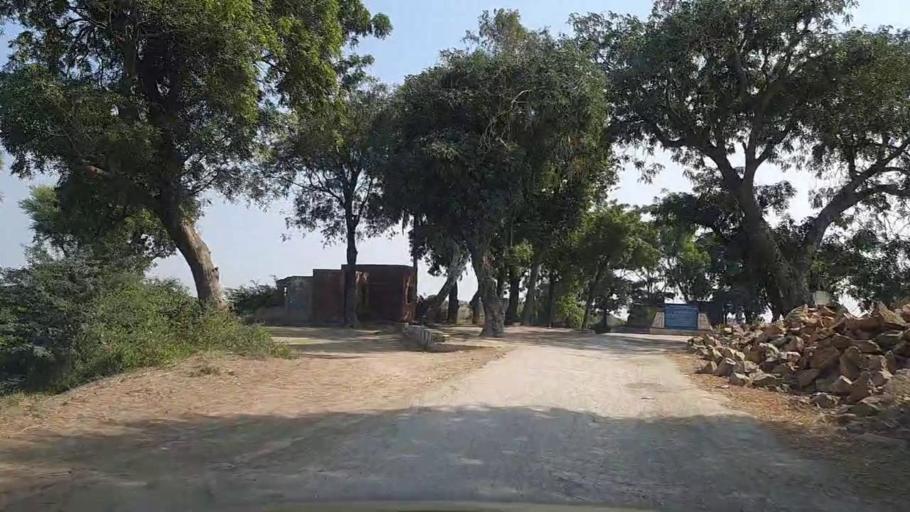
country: PK
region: Sindh
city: Thatta
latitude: 24.5802
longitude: 67.8984
